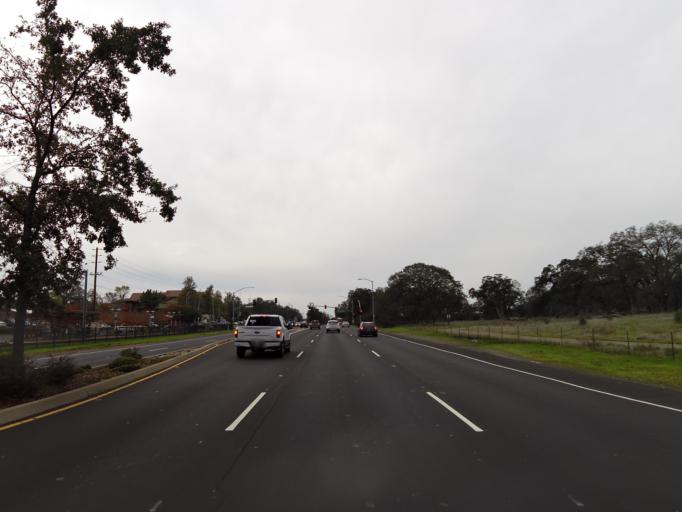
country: US
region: California
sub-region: Sacramento County
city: Folsom
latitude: 38.6451
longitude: -121.1899
